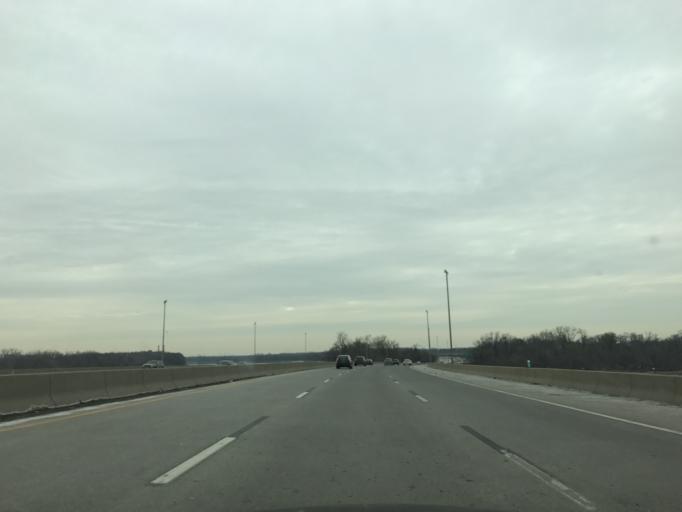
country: US
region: New Jersey
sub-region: Burlington County
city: Bordentown
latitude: 40.1473
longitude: -74.7194
